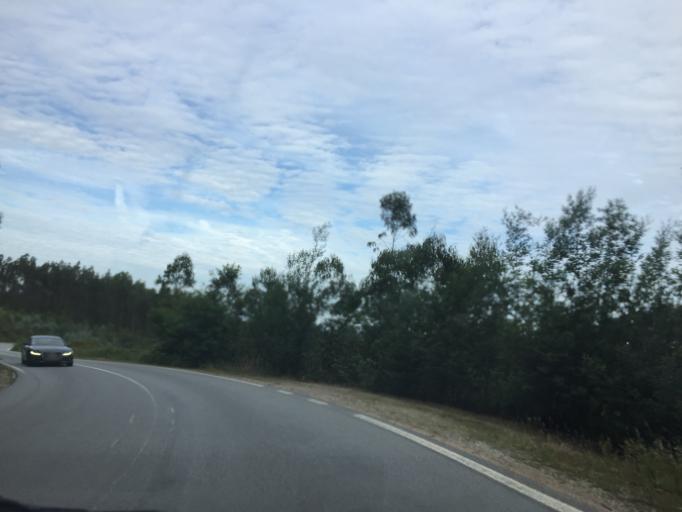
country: PT
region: Aveiro
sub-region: Agueda
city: Aguada de Cima
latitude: 40.4969
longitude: -8.3604
